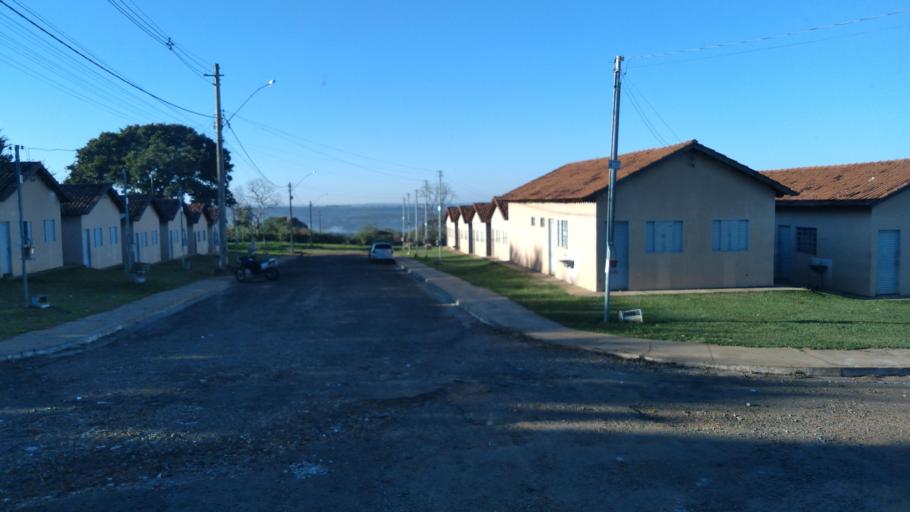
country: BR
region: Goias
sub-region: Mineiros
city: Mineiros
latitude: -17.5851
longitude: -52.5483
